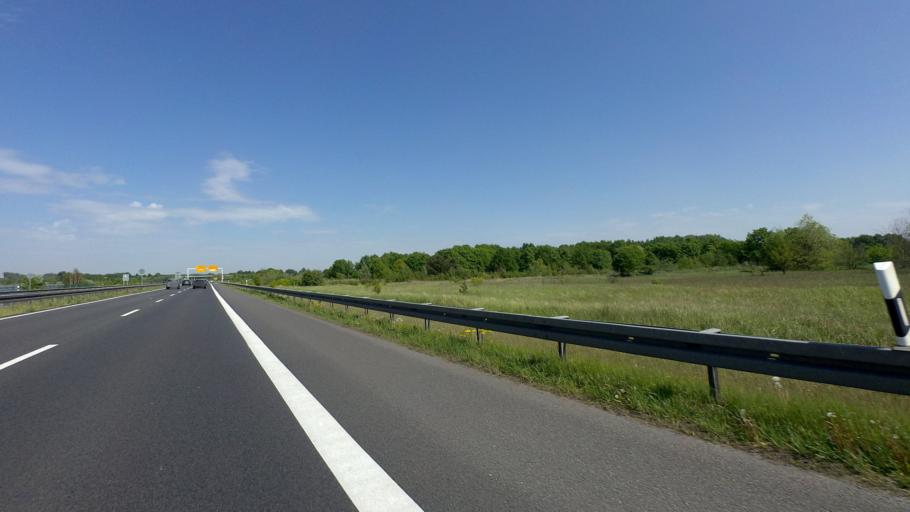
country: DE
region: Brandenburg
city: Leegebruch
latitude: 52.7336
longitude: 13.2113
